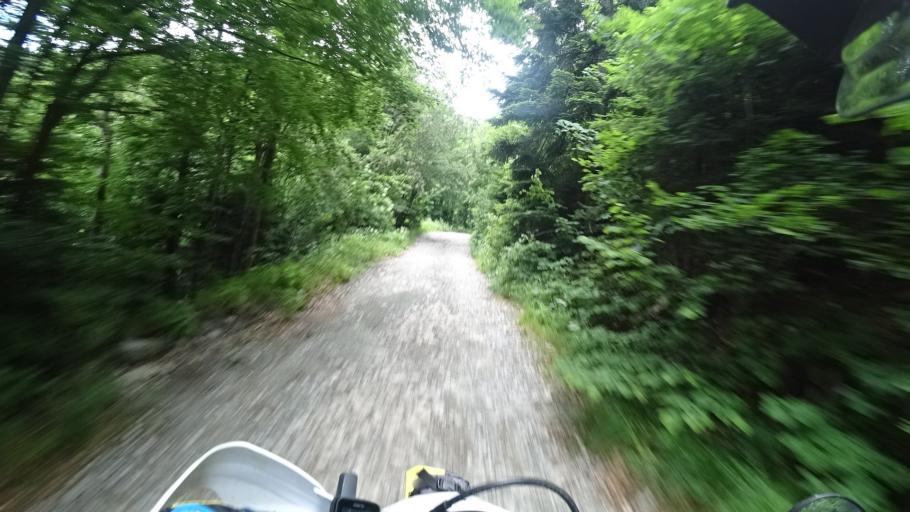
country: HR
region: Primorsko-Goranska
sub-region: Grad Crikvenica
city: Crikvenica
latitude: 45.2631
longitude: 14.7077
